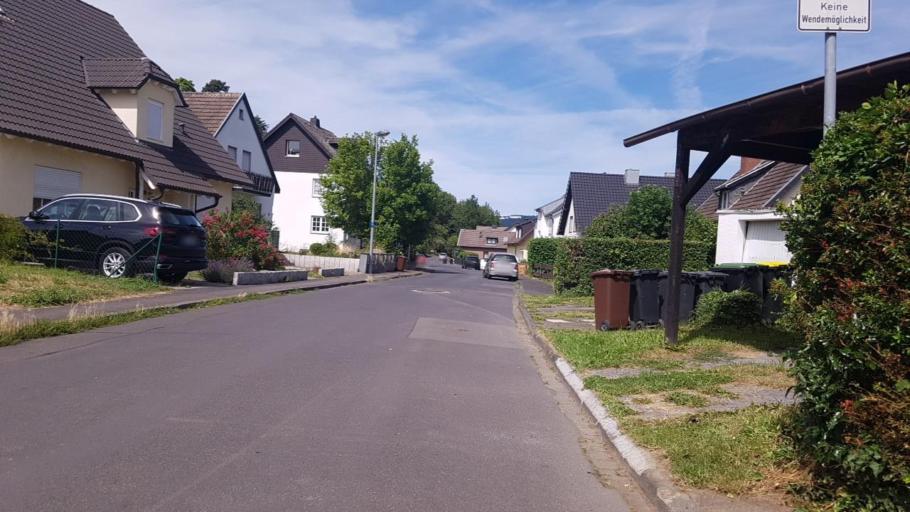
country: DE
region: North Rhine-Westphalia
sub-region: Regierungsbezirk Koln
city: Konigswinter
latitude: 50.6506
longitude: 7.1805
